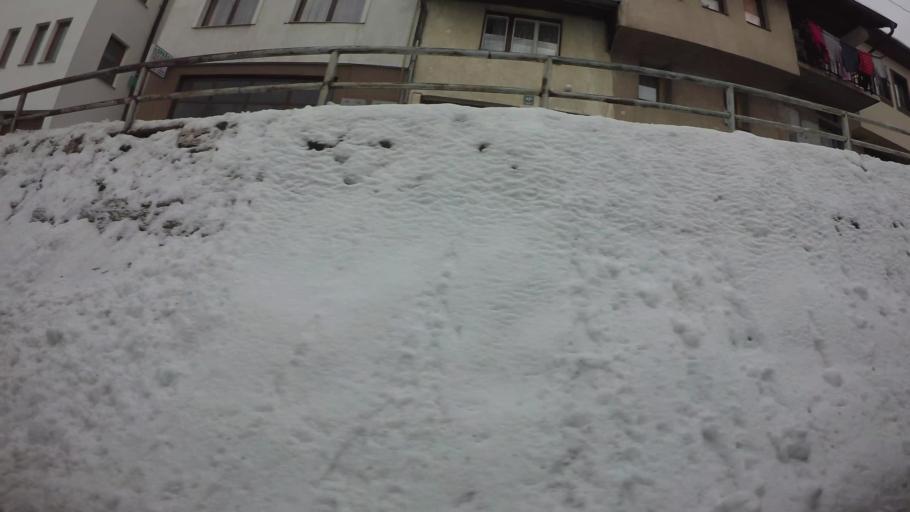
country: BA
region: Federation of Bosnia and Herzegovina
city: Kobilja Glava
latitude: 43.8622
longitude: 18.4449
